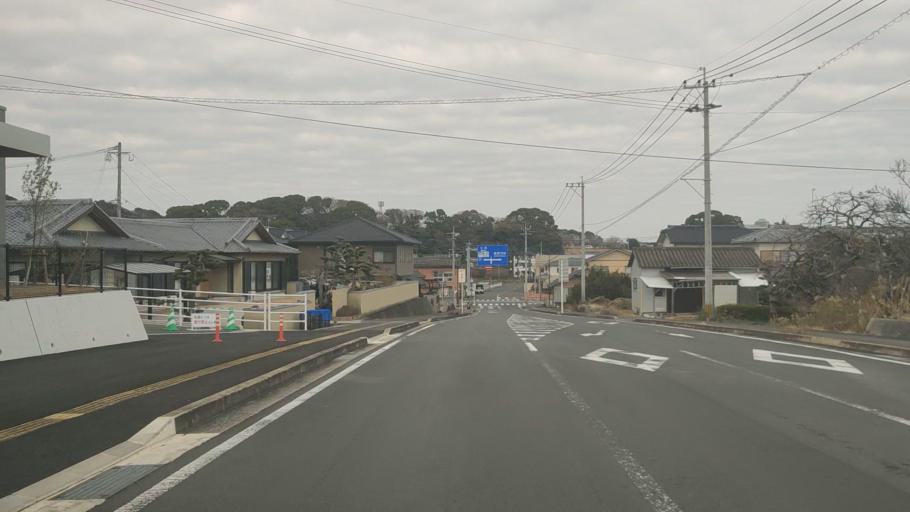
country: JP
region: Nagasaki
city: Shimabara
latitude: 32.7619
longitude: 130.3652
